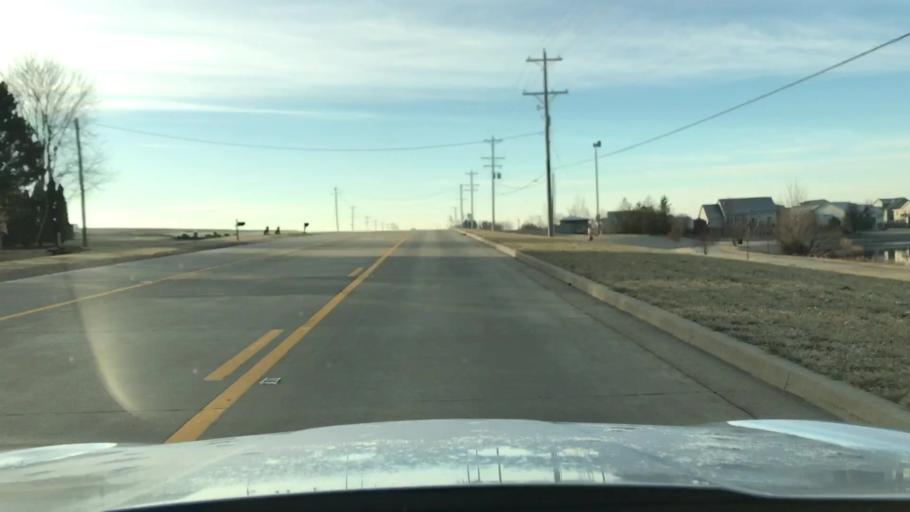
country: US
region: Illinois
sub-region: McLean County
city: Normal
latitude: 40.5550
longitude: -88.9446
